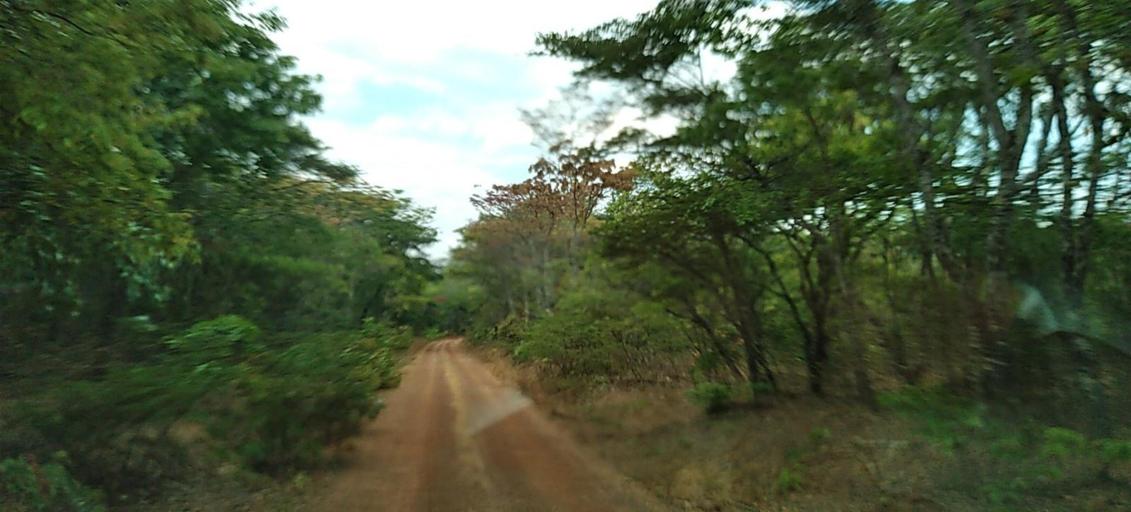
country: ZM
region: Copperbelt
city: Chililabombwe
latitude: -12.4512
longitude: 27.6127
